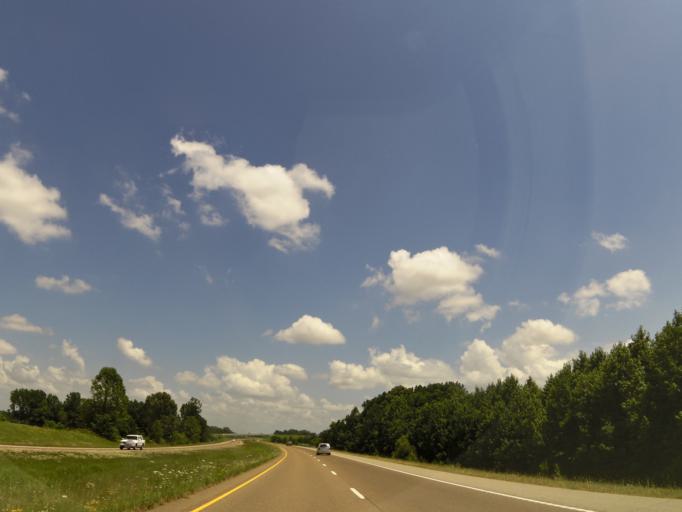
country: US
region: Tennessee
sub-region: Crockett County
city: Alamo
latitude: 35.7782
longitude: -89.1366
